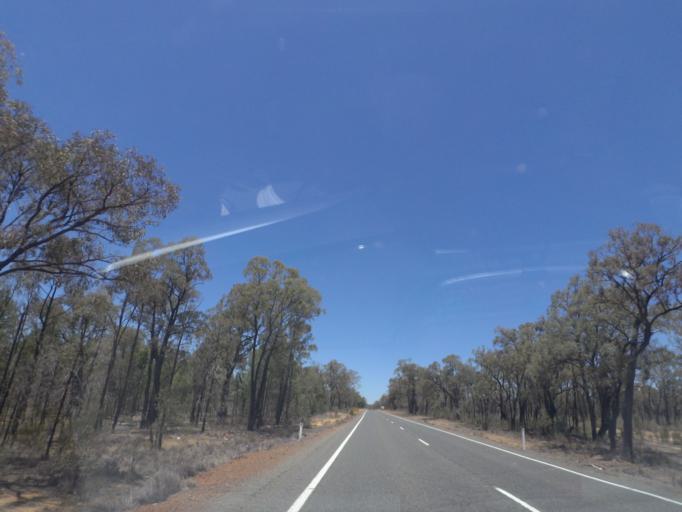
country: AU
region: New South Wales
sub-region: Narrabri
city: Narrabri
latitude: -30.7101
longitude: 149.5304
